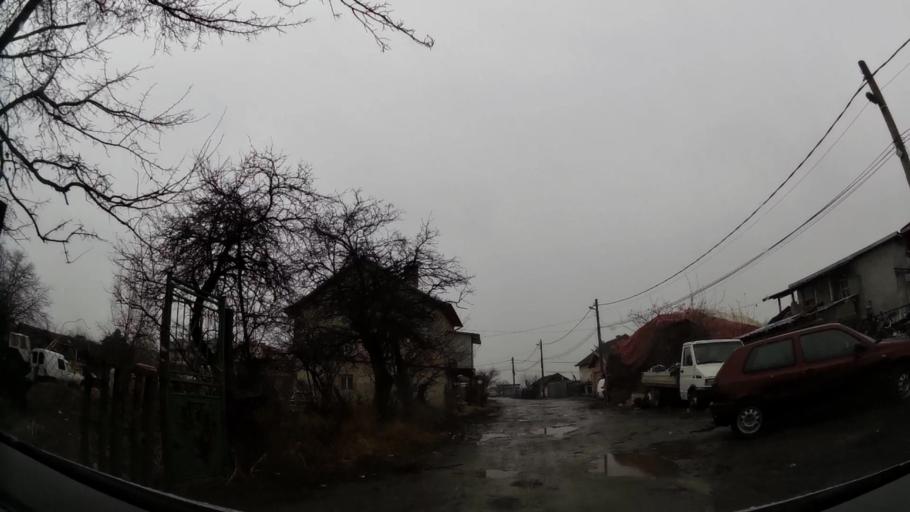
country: BG
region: Sofia-Capital
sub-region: Stolichna Obshtina
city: Sofia
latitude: 42.6627
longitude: 23.4278
